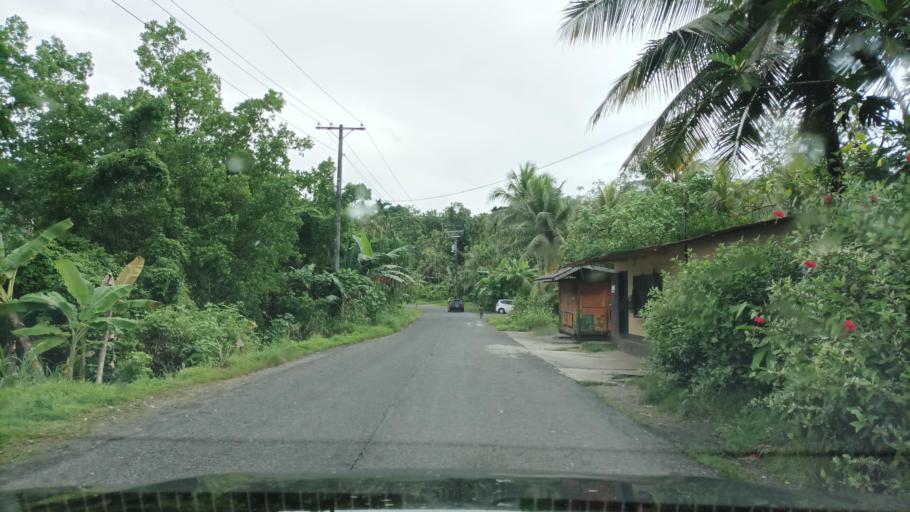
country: FM
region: Pohnpei
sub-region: Kolonia Municipality
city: Kolonia
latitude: 6.9296
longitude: 158.2784
